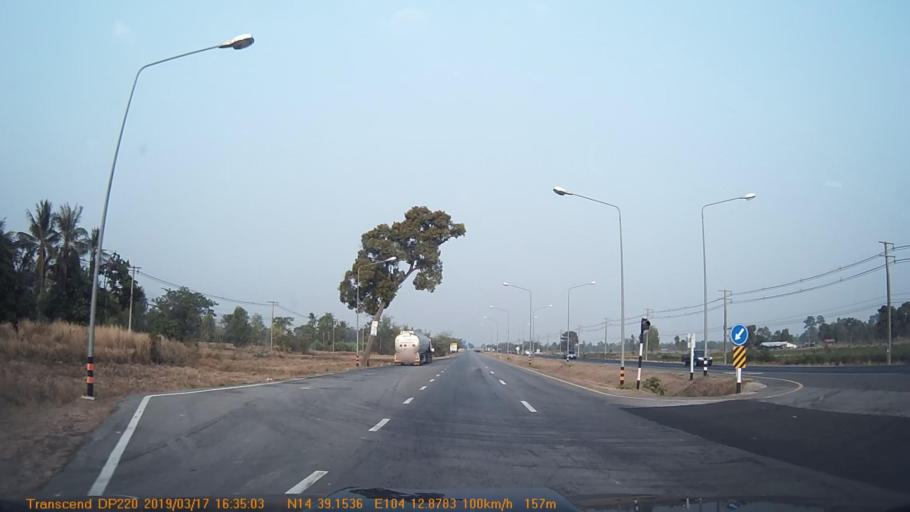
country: TH
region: Sisaket
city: Khu Khan
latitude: 14.6526
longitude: 104.2150
